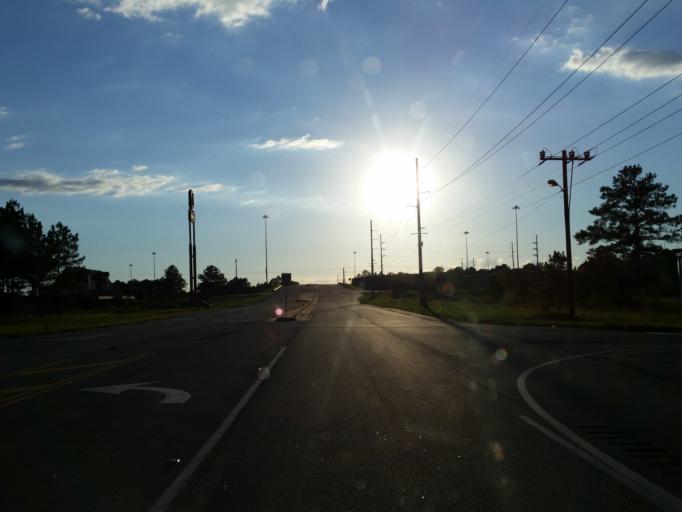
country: US
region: Georgia
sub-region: Crisp County
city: Cordele
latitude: 32.0052
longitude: -83.7545
